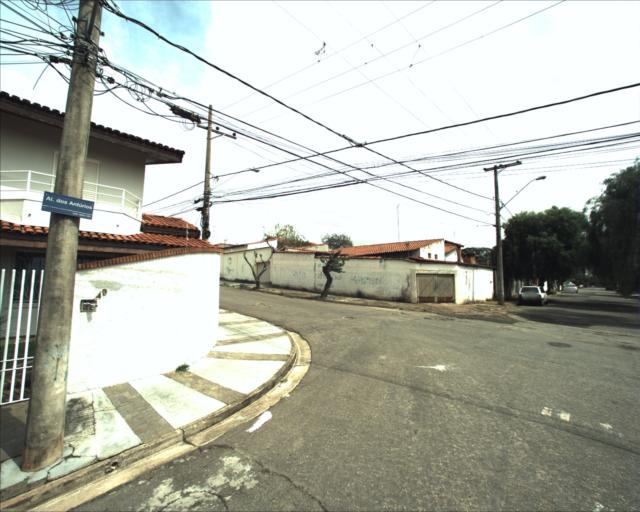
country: BR
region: Sao Paulo
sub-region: Sorocaba
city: Sorocaba
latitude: -23.5011
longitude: -47.4927
